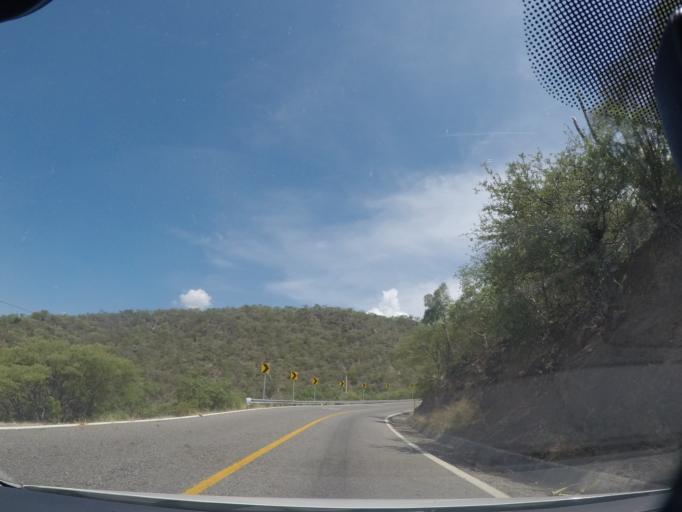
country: MX
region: Oaxaca
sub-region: San Juan del Rio
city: San Juan del Rio
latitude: 16.6958
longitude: -96.2037
